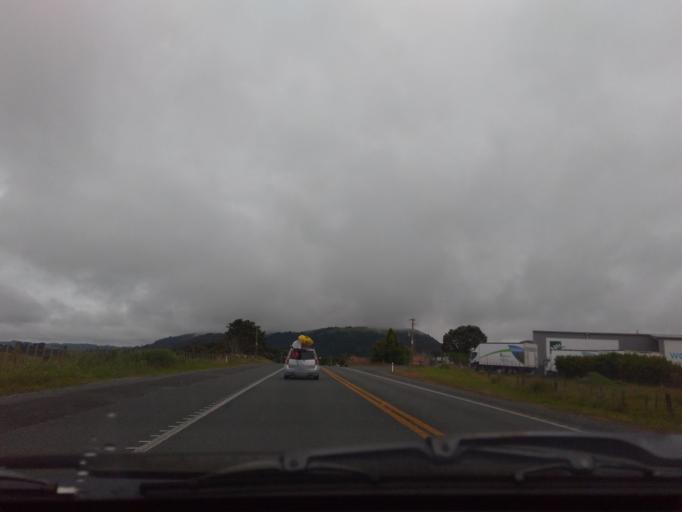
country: NZ
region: Auckland
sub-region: Auckland
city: Wellsford
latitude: -36.1438
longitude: 174.4359
